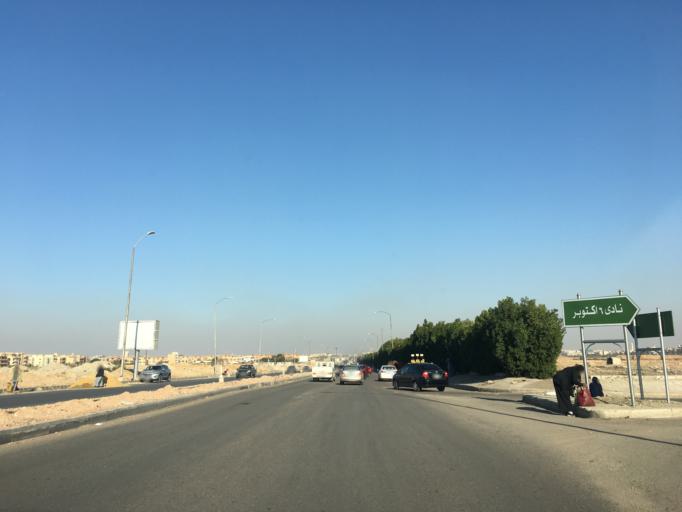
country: EG
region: Al Jizah
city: Madinat Sittah Uktubar
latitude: 29.9888
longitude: 30.9421
